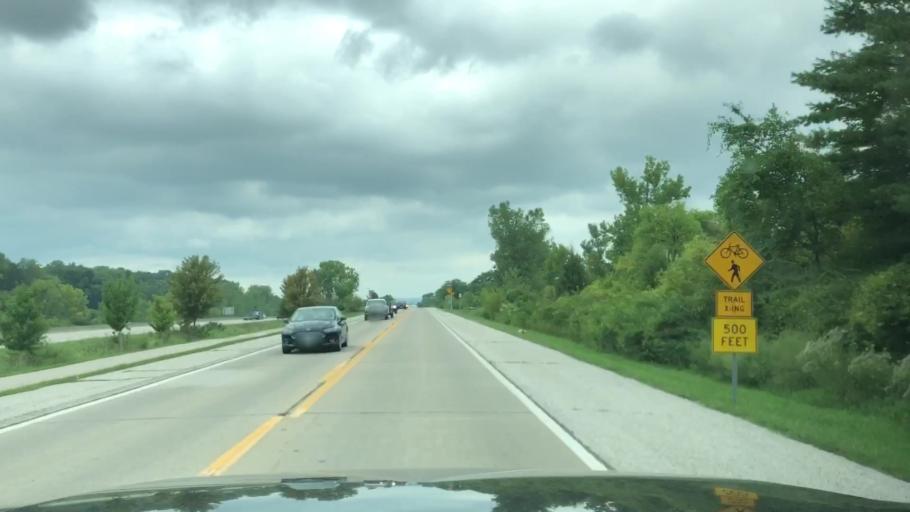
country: US
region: Missouri
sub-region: Saint Charles County
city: Saint Charles
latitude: 38.8143
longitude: -90.4908
